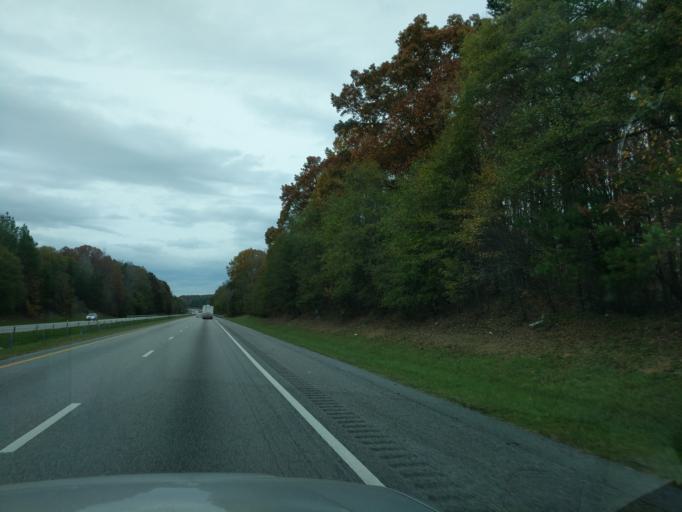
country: US
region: South Carolina
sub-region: Laurens County
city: Clinton
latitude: 34.5888
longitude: -81.8923
